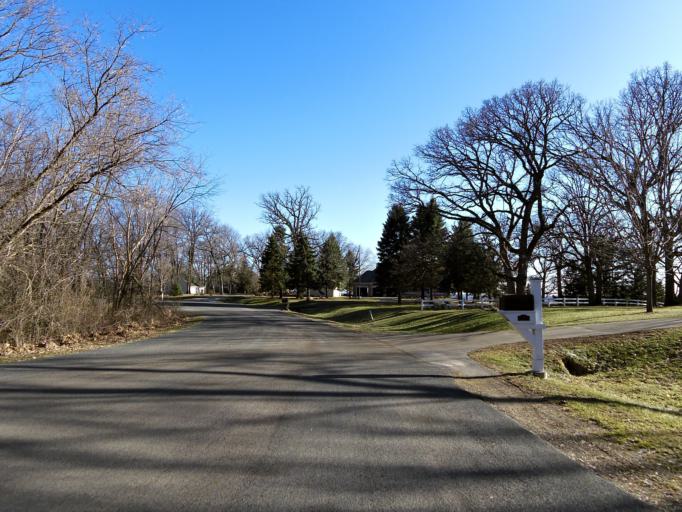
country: US
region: Minnesota
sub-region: Washington County
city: Lakeland
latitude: 44.9817
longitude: -92.8023
